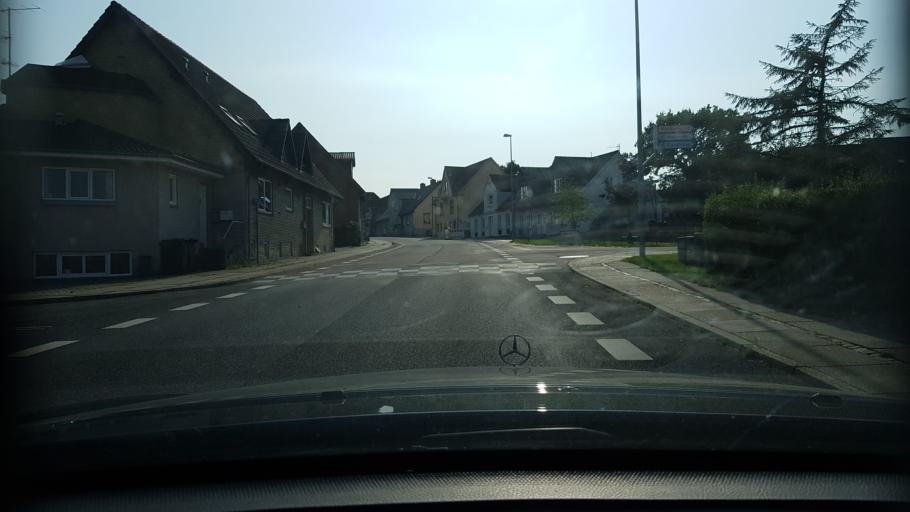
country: DK
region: North Denmark
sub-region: Mariagerfjord Kommune
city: Hadsund
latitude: 56.7216
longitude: 10.1197
